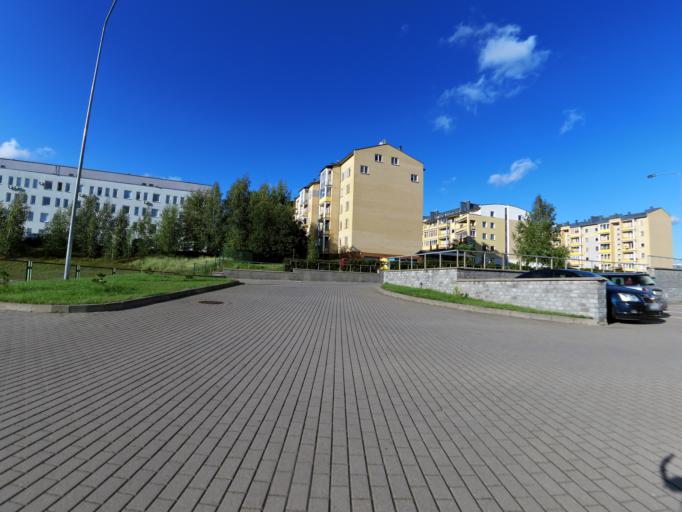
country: LT
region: Vilnius County
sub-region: Vilnius
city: Fabijoniskes
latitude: 54.7216
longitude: 25.2387
